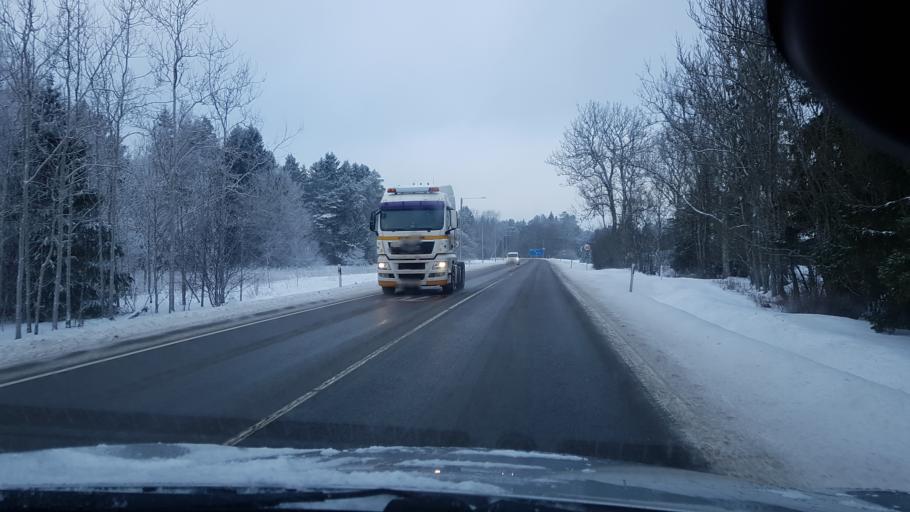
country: EE
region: Harju
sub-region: Keila linn
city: Keila
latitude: 59.3389
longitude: 24.2722
